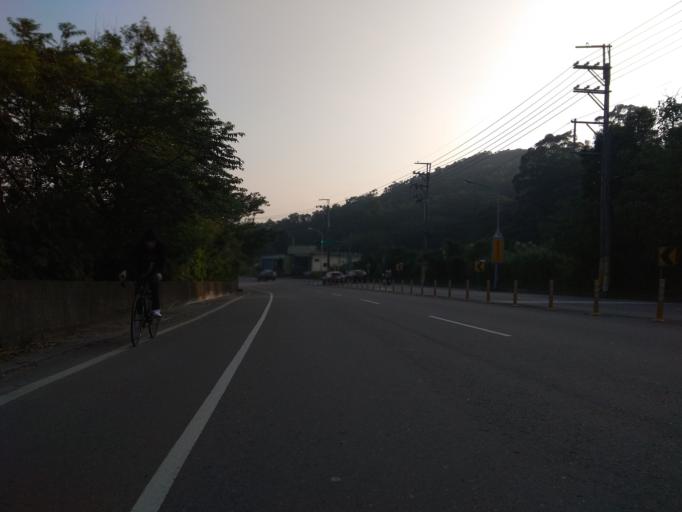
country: TW
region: Taiwan
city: Daxi
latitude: 24.9082
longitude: 121.1884
